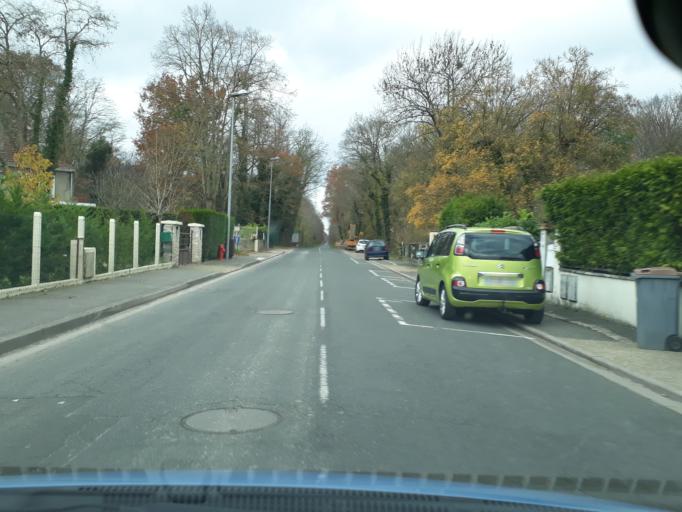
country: FR
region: Ile-de-France
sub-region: Departement de Seine-et-Marne
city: Veneux-les-Sablons
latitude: 48.3862
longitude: 2.7803
